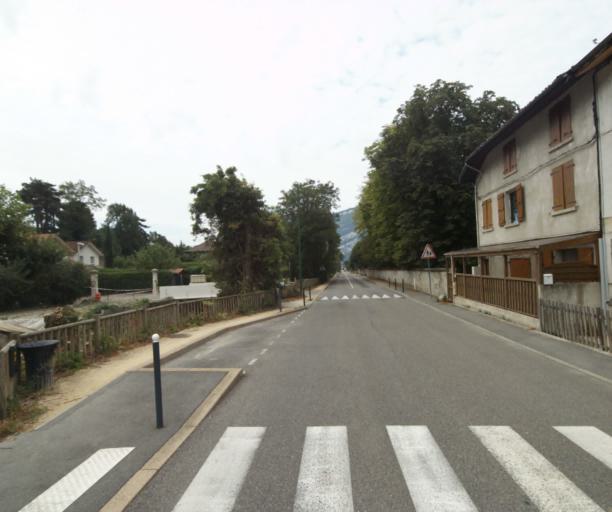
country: FR
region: Rhone-Alpes
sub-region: Departement de l'Isere
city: Saint-Egreve
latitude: 45.2369
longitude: 5.6895
